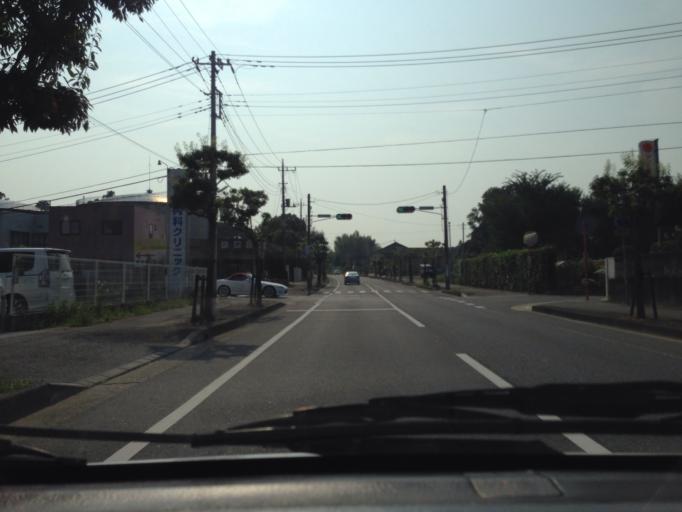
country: JP
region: Ibaraki
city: Ami
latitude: 36.0594
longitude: 140.2059
